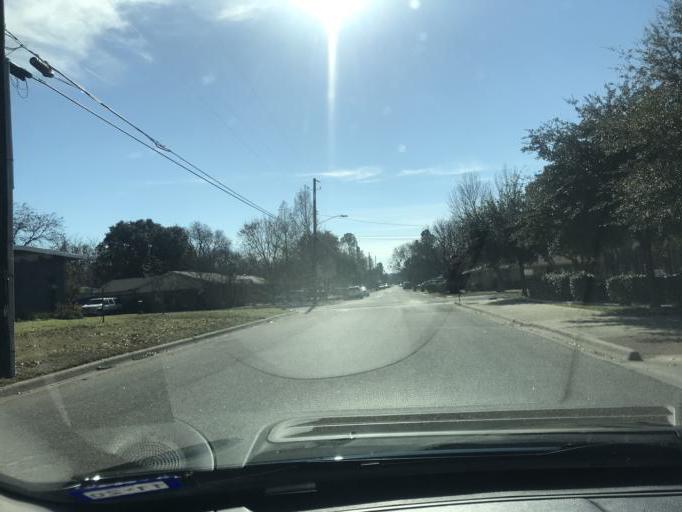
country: US
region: Texas
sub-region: Denton County
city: Denton
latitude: 33.2291
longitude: -97.1359
